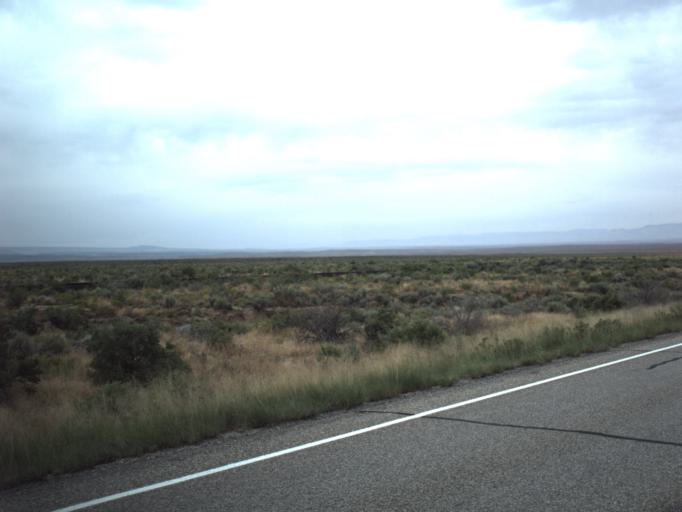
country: US
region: Utah
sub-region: Carbon County
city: East Carbon City
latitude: 39.5348
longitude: -110.5154
